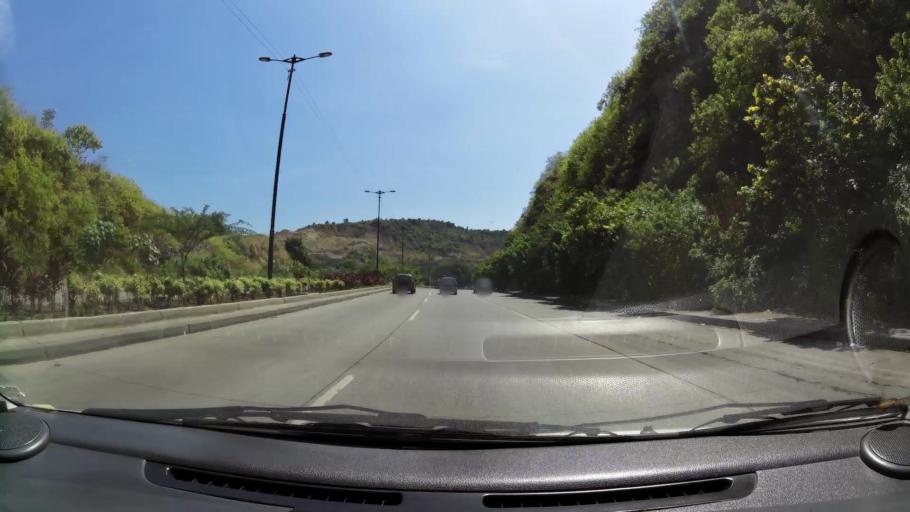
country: EC
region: Guayas
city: Guayaquil
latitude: -2.1890
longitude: -79.9324
